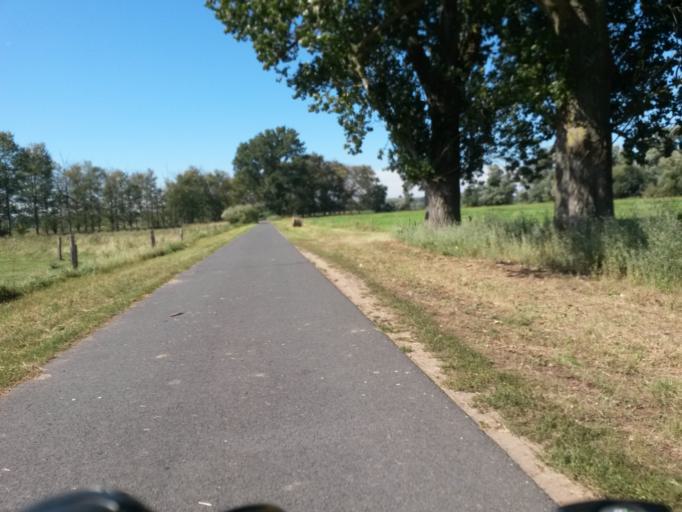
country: PL
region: West Pomeranian Voivodeship
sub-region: Powiat gryfinski
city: Cedynia
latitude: 52.9212
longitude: 14.1395
